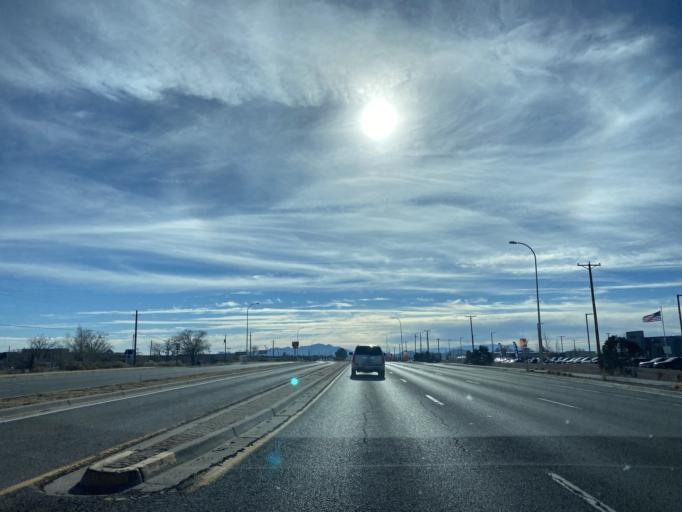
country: US
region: New Mexico
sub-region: Santa Fe County
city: Agua Fria
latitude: 35.6245
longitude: -106.0264
